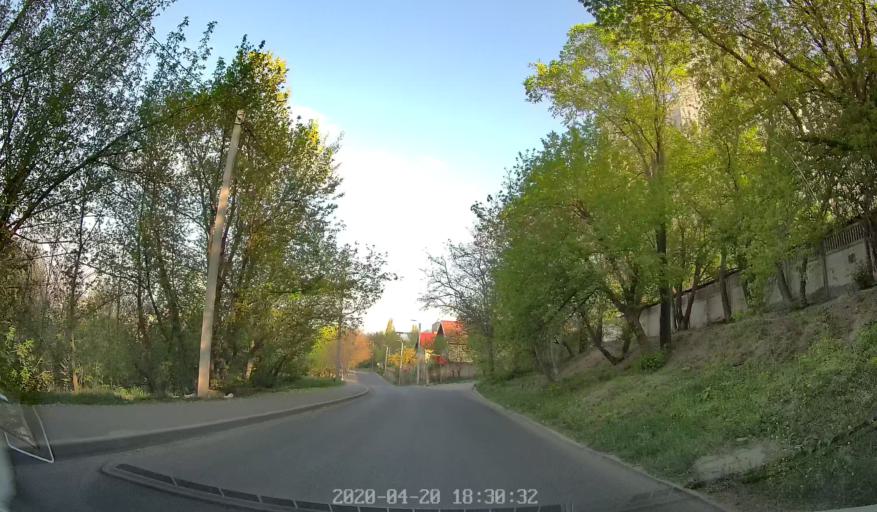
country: MD
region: Chisinau
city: Chisinau
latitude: 46.9881
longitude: 28.8360
